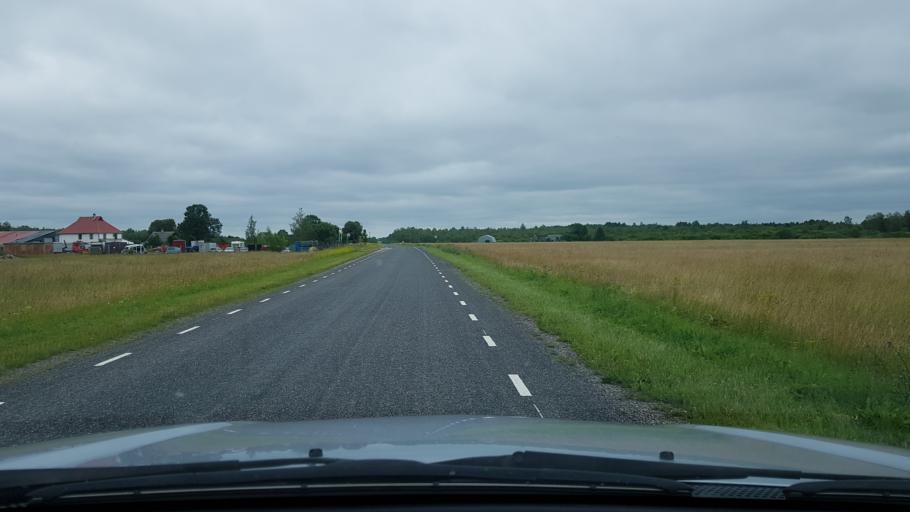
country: EE
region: Ida-Virumaa
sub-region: Narva linn
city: Narva
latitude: 59.3726
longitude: 28.1033
